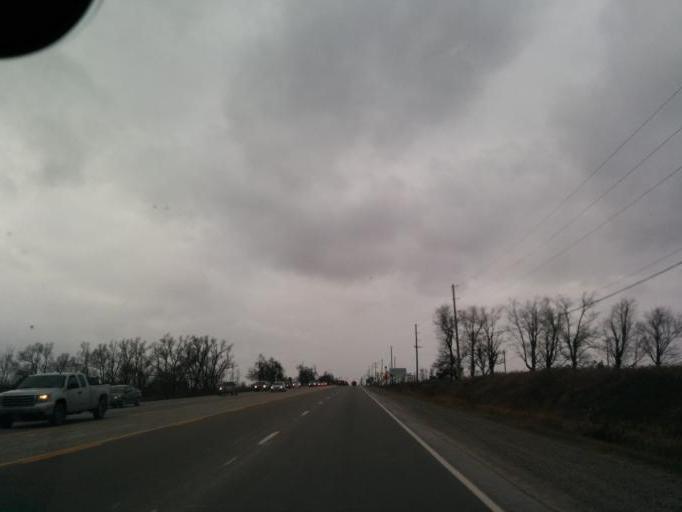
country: CA
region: Ontario
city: Brampton
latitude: 43.7507
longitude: -79.8476
